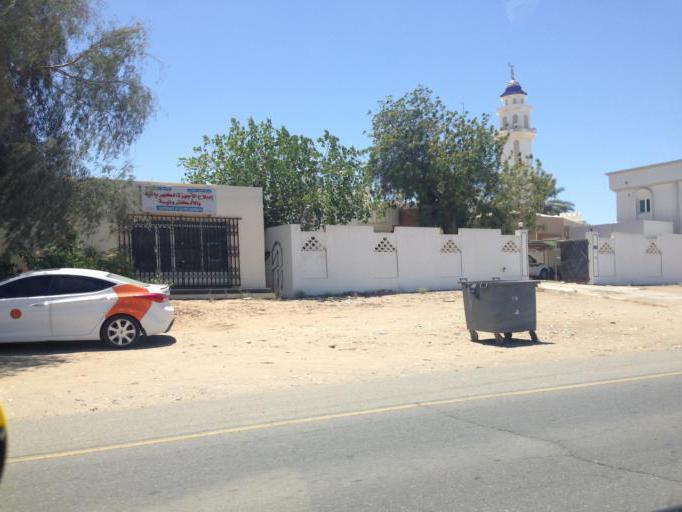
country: OM
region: Muhafazat Masqat
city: As Sib al Jadidah
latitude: 23.6445
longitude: 58.2351
